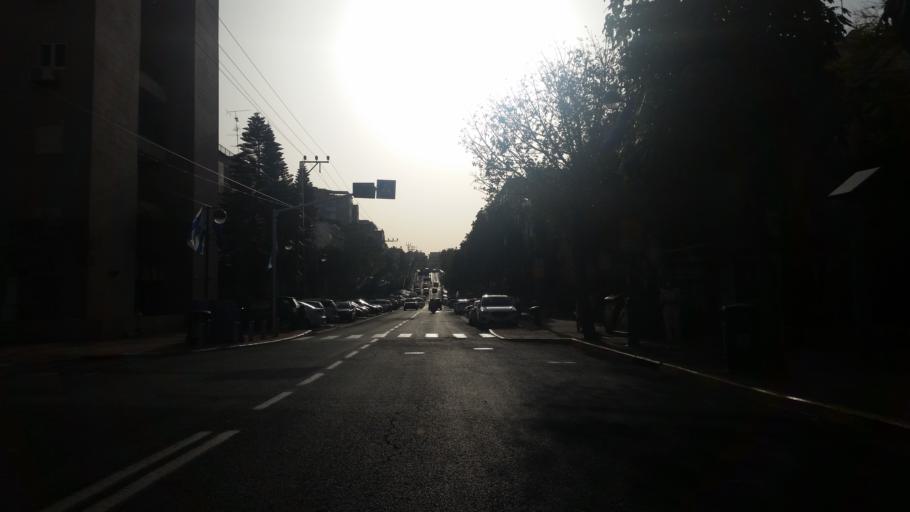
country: IL
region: Tel Aviv
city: Bene Beraq
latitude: 32.0749
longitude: 34.8323
